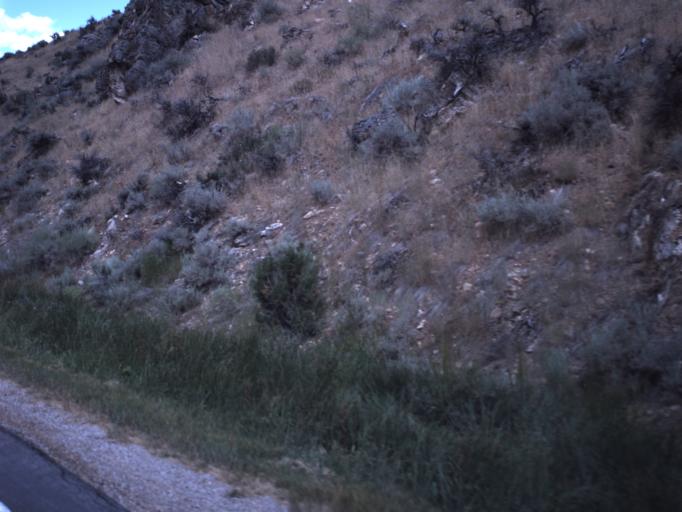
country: US
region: Utah
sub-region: Rich County
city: Randolph
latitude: 41.8221
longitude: -111.2910
